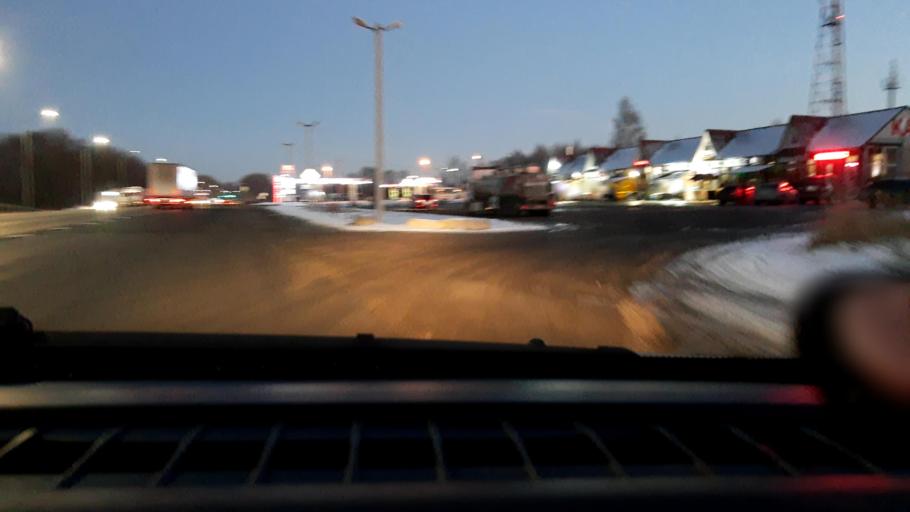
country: RU
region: Nizjnij Novgorod
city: Lyskovo
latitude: 56.0151
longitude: 45.0126
